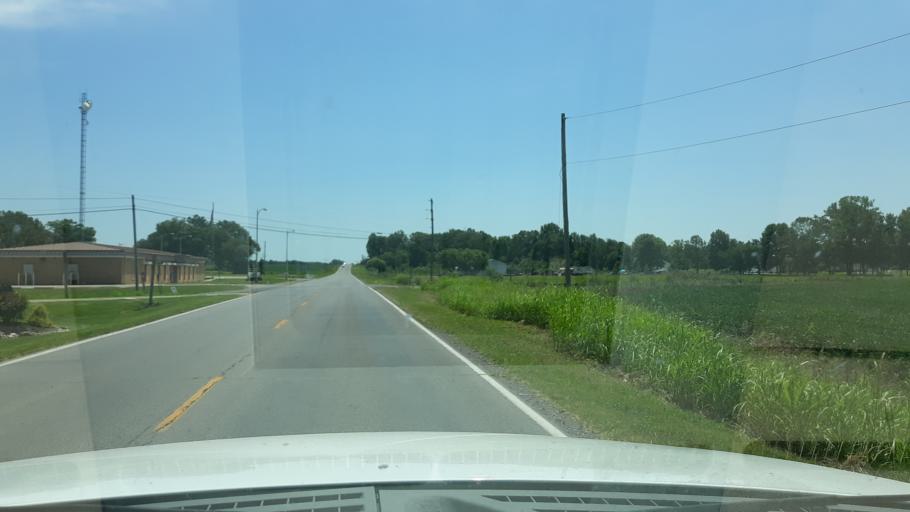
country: US
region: Illinois
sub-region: Saline County
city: Eldorado
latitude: 37.8036
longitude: -88.4329
